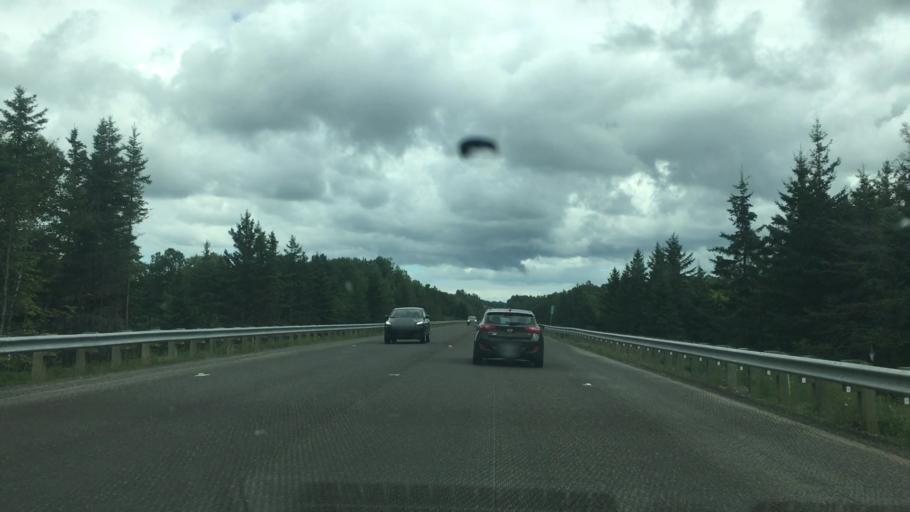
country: CA
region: Nova Scotia
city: Antigonish
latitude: 45.5858
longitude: -62.0827
